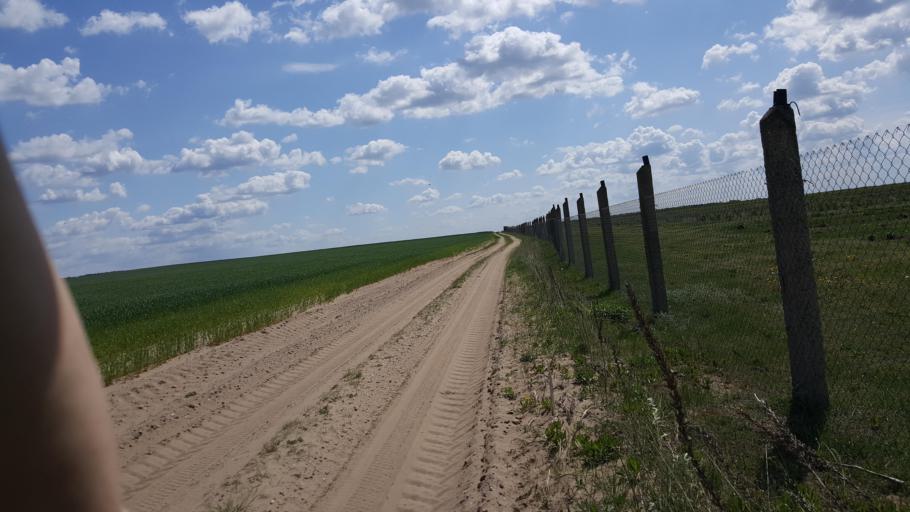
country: BY
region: Brest
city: Kamyanyets
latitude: 52.3815
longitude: 23.9099
